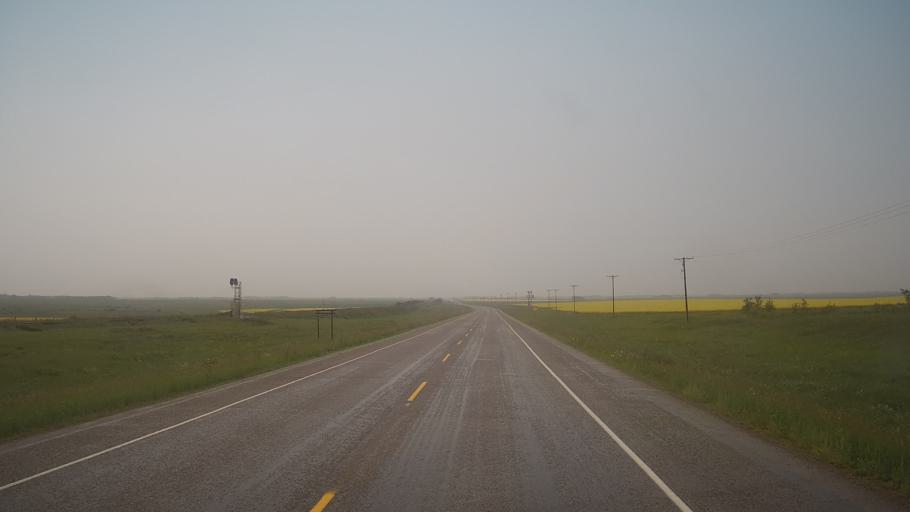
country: CA
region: Saskatchewan
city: Biggar
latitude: 52.1426
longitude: -108.1950
